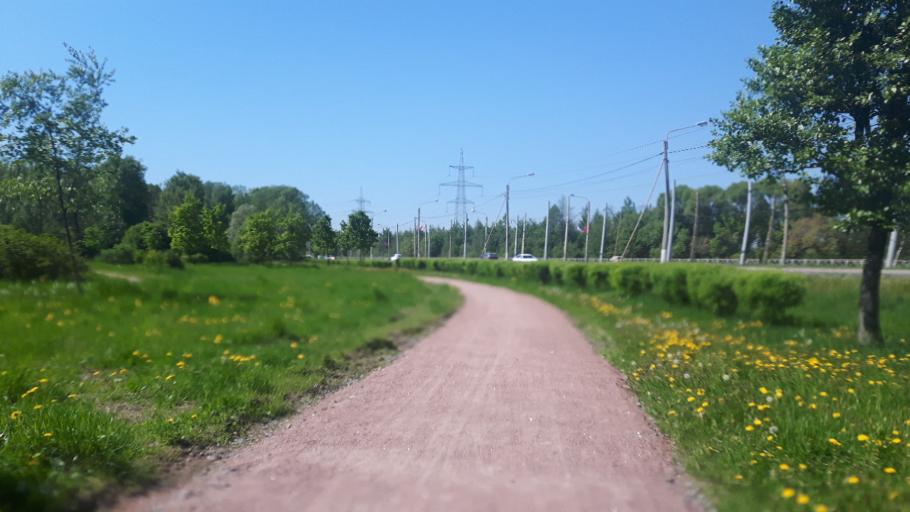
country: RU
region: St.-Petersburg
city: Sosnovaya Polyana
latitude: 59.8517
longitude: 30.1132
